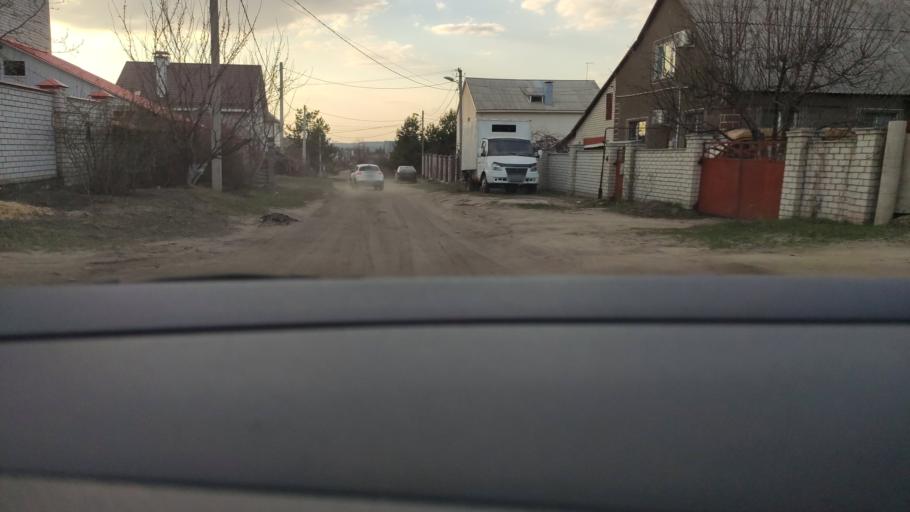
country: RU
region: Voronezj
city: Pridonskoy
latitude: 51.6291
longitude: 39.0933
